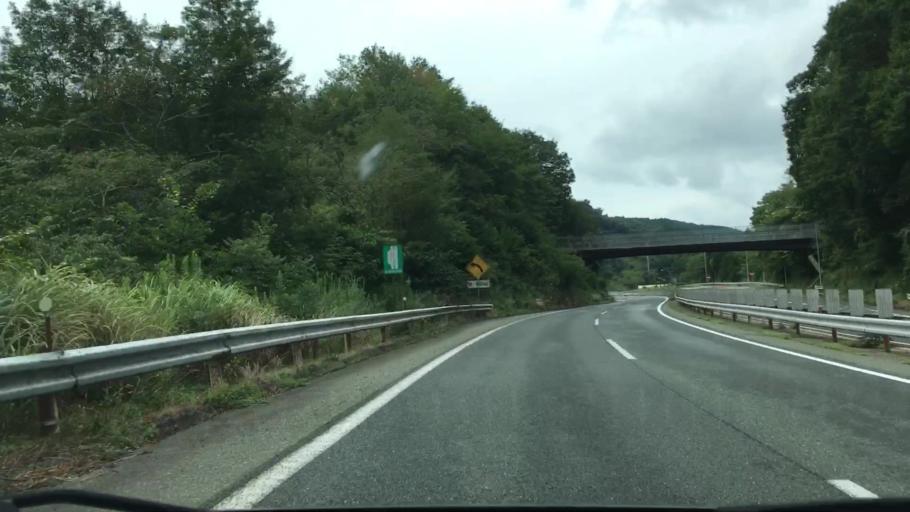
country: JP
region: Okayama
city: Niimi
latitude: 34.8939
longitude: 133.2492
